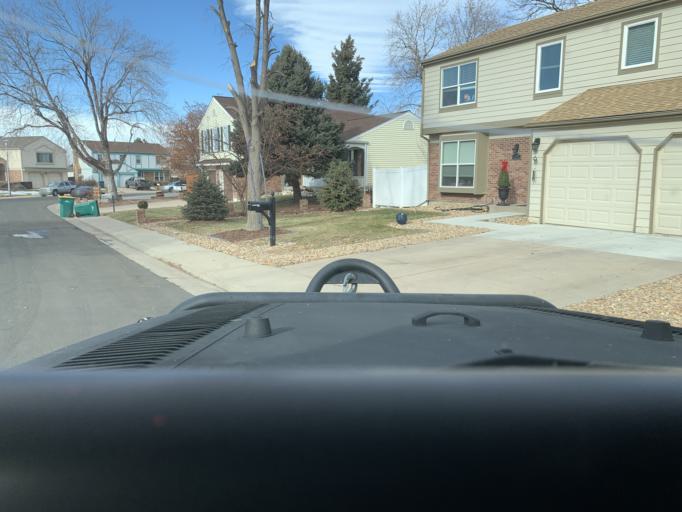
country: US
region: Colorado
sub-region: Adams County
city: Aurora
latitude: 39.7021
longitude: -104.7989
